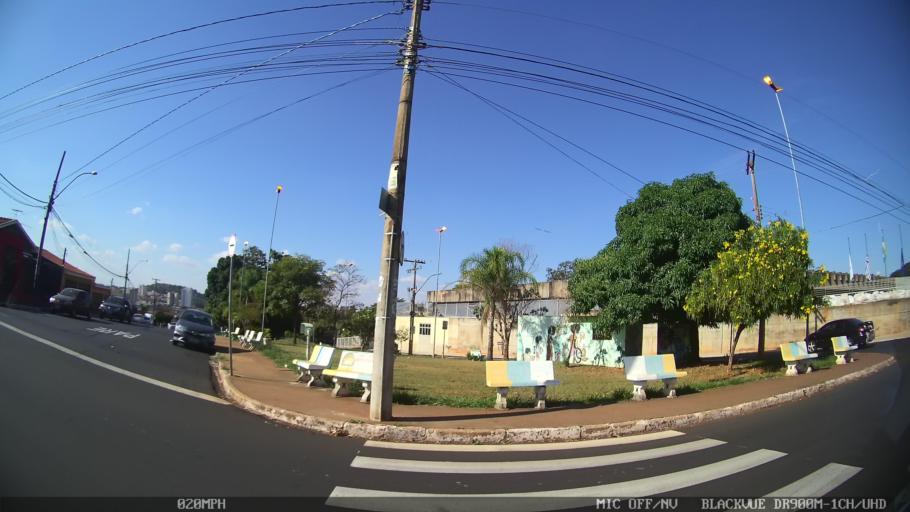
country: BR
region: Sao Paulo
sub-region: Ribeirao Preto
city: Ribeirao Preto
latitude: -21.1898
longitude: -47.7781
